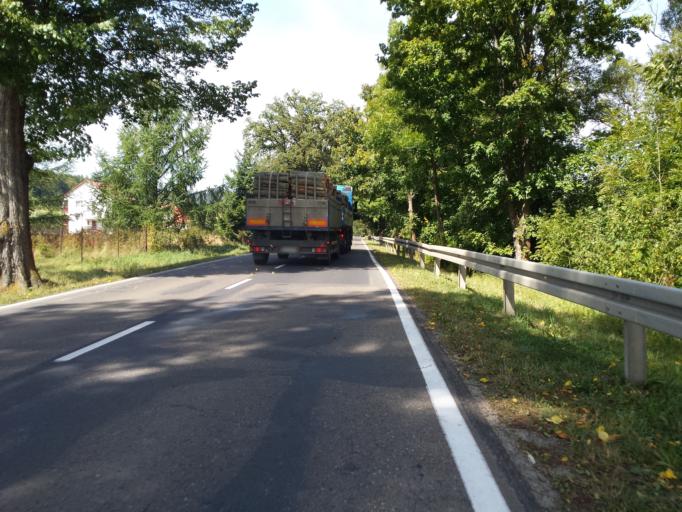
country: PL
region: Subcarpathian Voivodeship
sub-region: Powiat leski
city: Lesko
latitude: 49.4593
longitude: 22.3357
